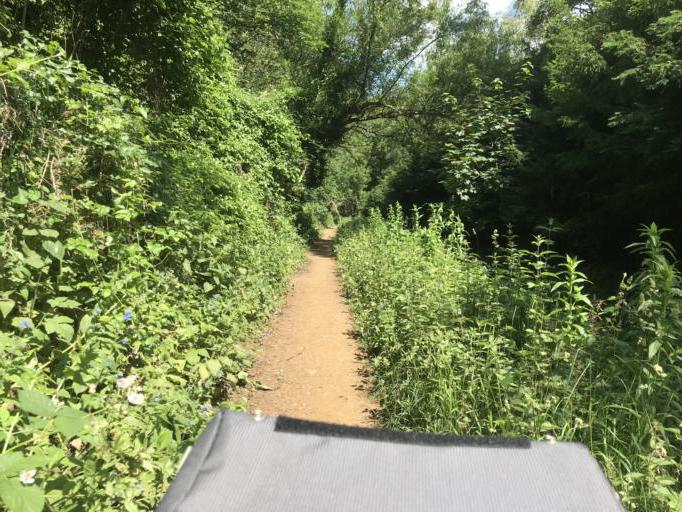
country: GB
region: England
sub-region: Cambridgeshire
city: Cambridge
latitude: 52.1867
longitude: 0.1272
